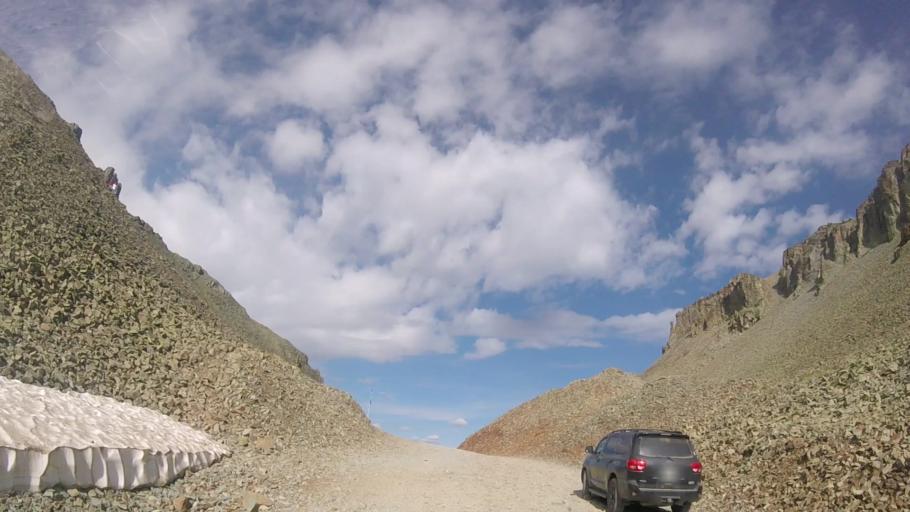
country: US
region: Colorado
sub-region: San Miguel County
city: Telluride
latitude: 37.8509
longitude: -107.7788
